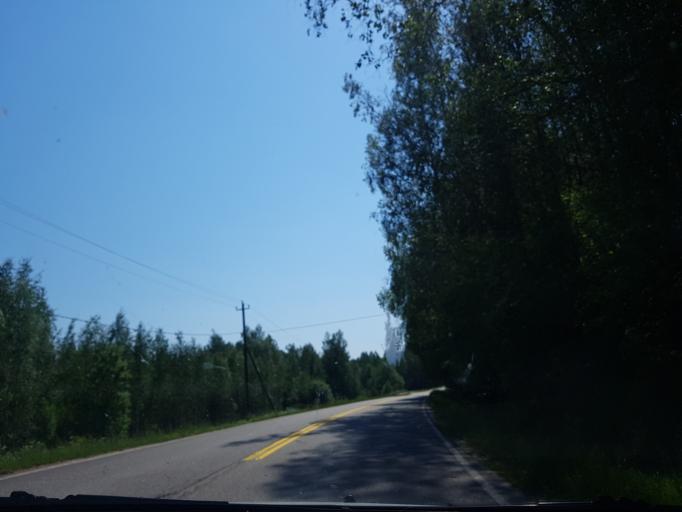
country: FI
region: Uusimaa
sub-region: Helsinki
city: Vihti
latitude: 60.3121
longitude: 24.4032
